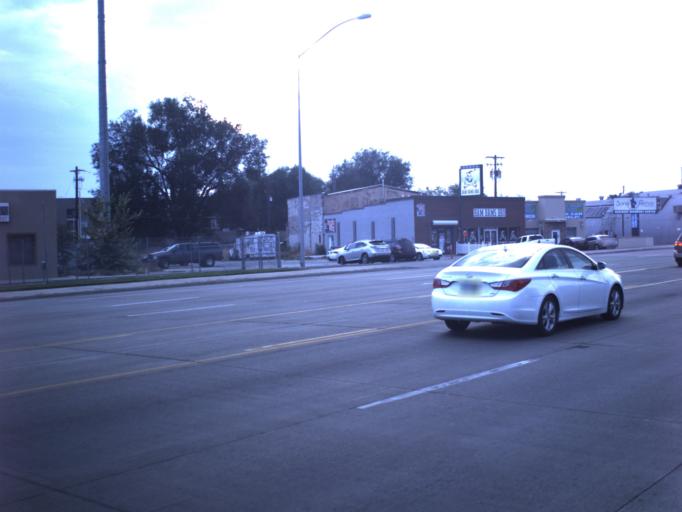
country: US
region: Utah
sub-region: Utah County
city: Orem
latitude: 40.2654
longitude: -111.6806
